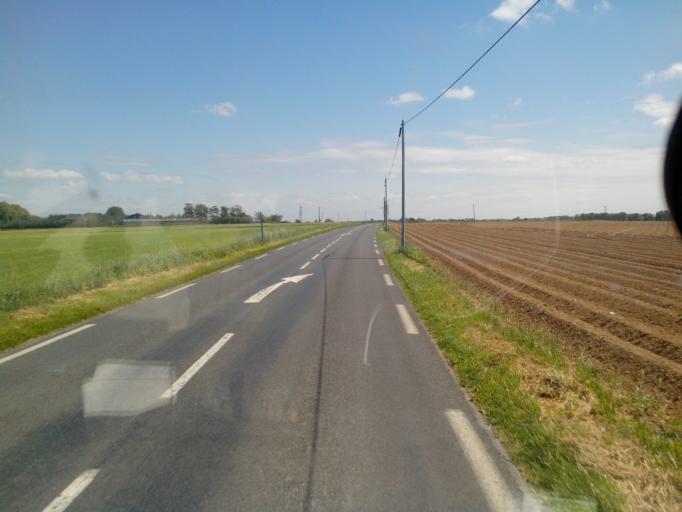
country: FR
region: Haute-Normandie
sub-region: Departement de la Seine-Maritime
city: Ecrainville
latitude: 49.6156
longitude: 0.2861
